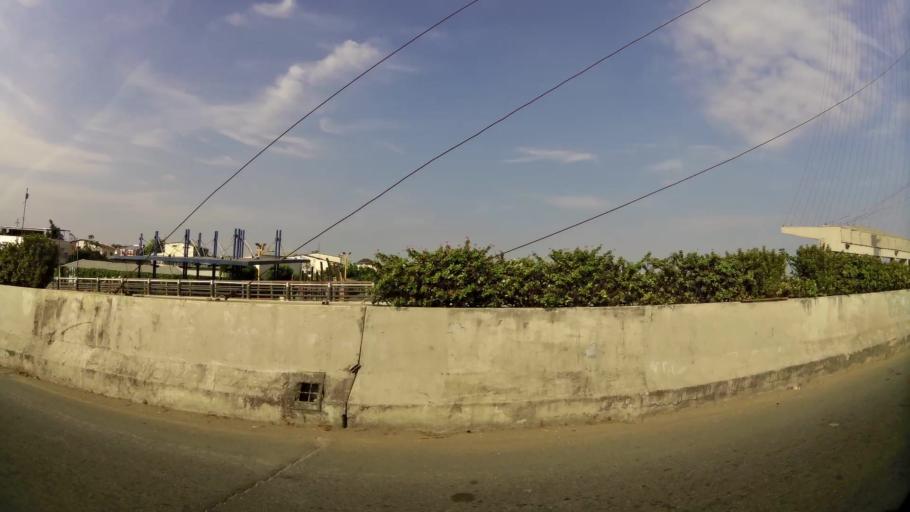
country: EC
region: Guayas
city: Guayaquil
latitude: -2.1891
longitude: -79.9011
